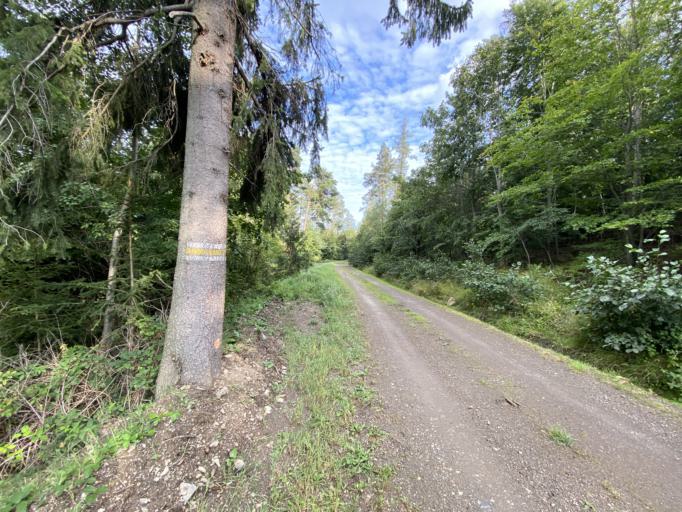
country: AT
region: Burgenland
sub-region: Politischer Bezirk Oberpullendorf
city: Kobersdorf
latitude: 47.5828
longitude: 16.3490
